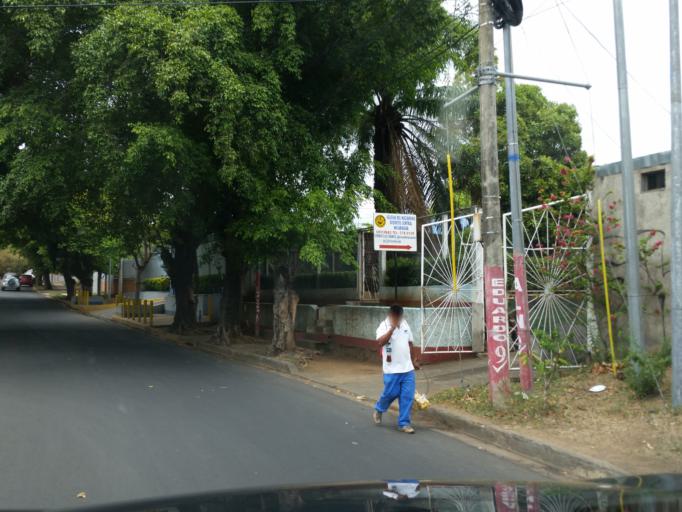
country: NI
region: Managua
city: Managua
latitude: 12.1266
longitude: -86.2687
